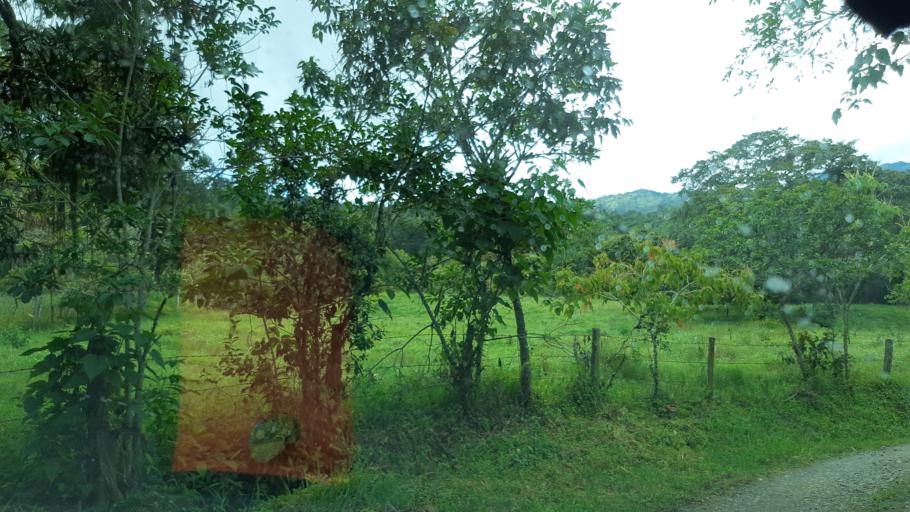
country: CO
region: Boyaca
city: Garagoa
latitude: 5.0373
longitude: -73.3566
